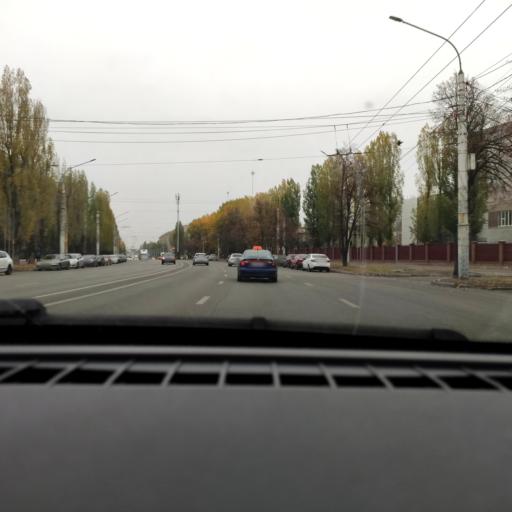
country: RU
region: Voronezj
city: Voronezh
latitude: 51.6770
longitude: 39.2582
